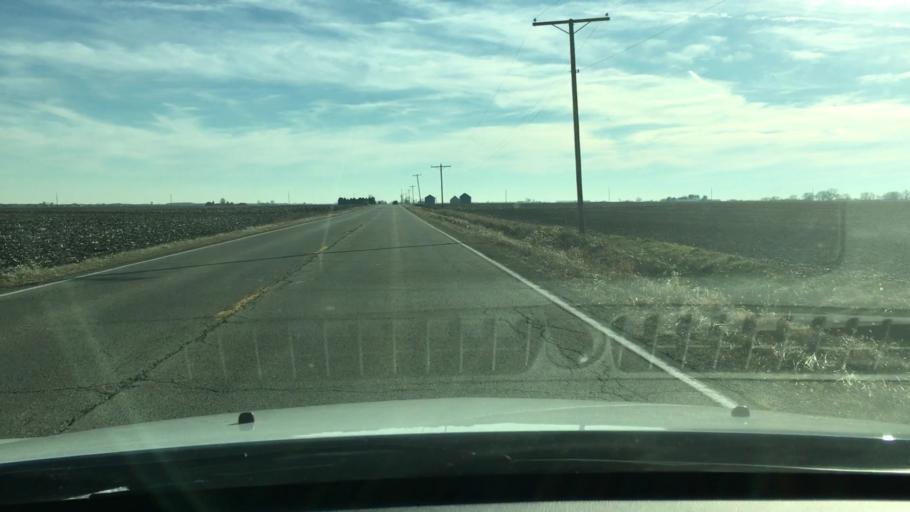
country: US
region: Illinois
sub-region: LaSalle County
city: Mendota
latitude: 41.4487
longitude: -89.1268
